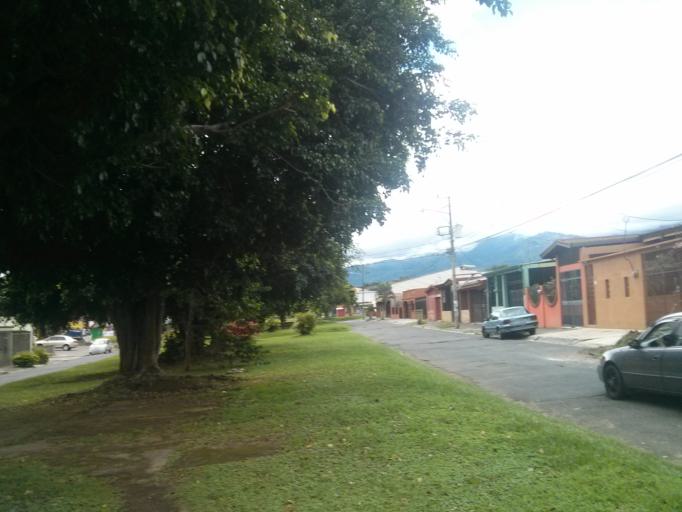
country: CR
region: San Jose
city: Curridabat
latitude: 9.8998
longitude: -84.0539
